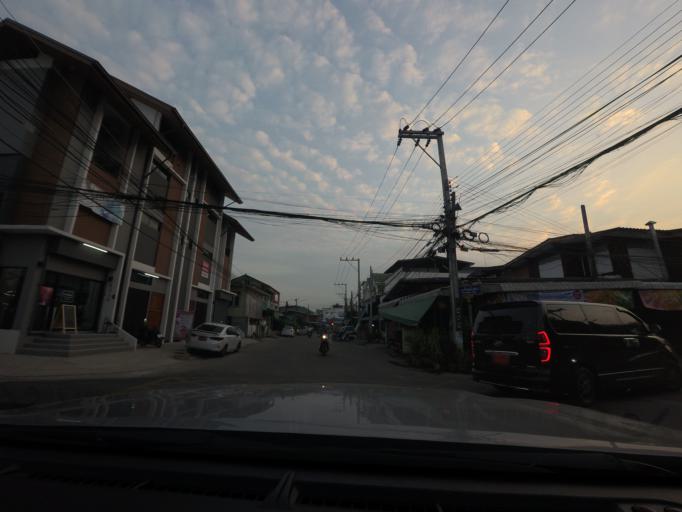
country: TH
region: Phitsanulok
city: Phitsanulok
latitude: 16.8197
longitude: 100.2757
